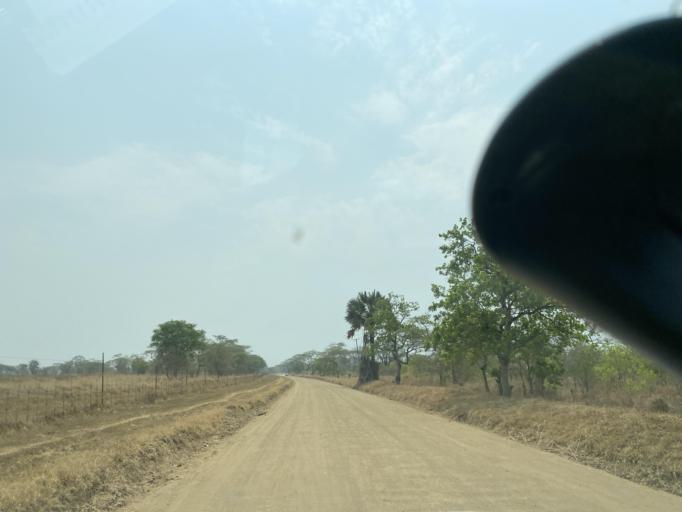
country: ZM
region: Lusaka
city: Kafue
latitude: -15.5933
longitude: 28.1135
